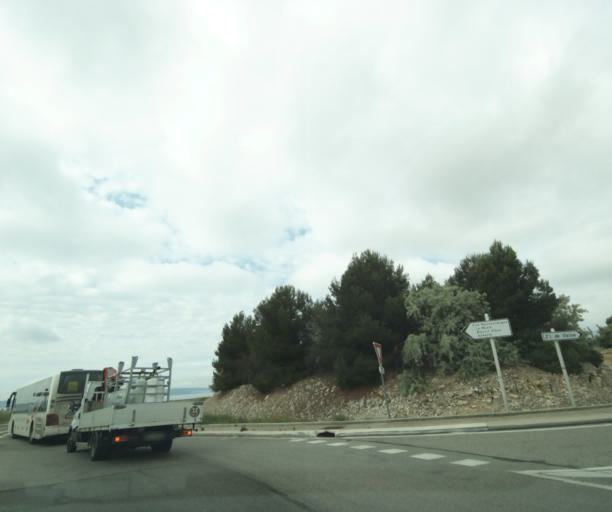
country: FR
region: Provence-Alpes-Cote d'Azur
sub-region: Departement des Bouches-du-Rhone
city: Berre-l'Etang
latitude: 43.4901
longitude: 5.1986
